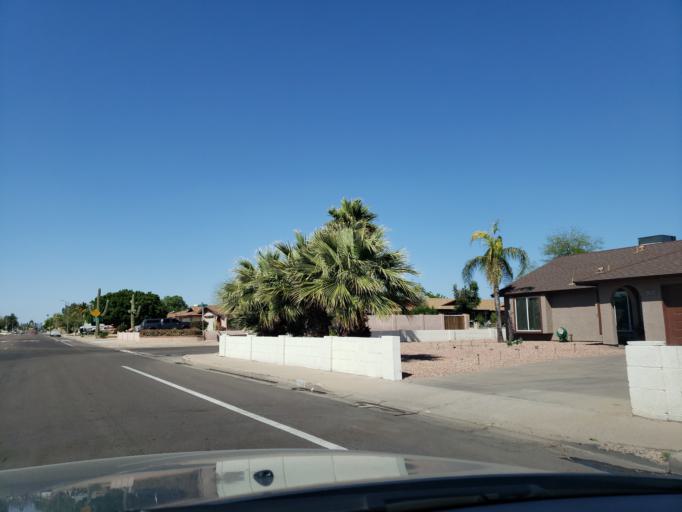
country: US
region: Arizona
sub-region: Maricopa County
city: Glendale
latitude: 33.5635
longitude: -112.1776
